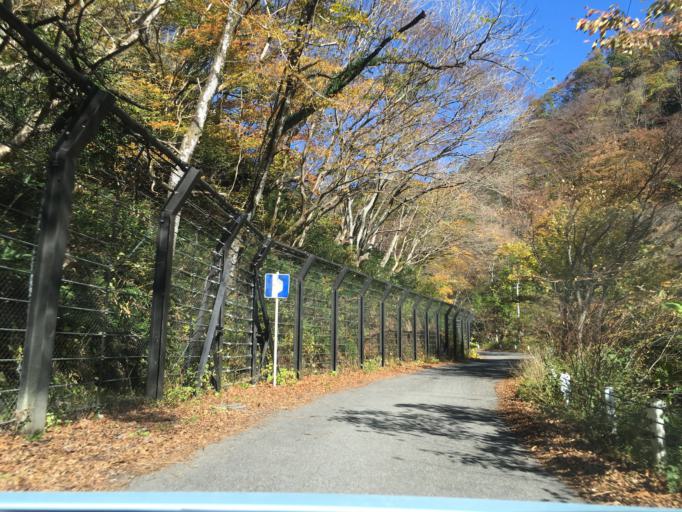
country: JP
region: Fukushima
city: Inawashiro
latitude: 37.4227
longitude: 139.9869
